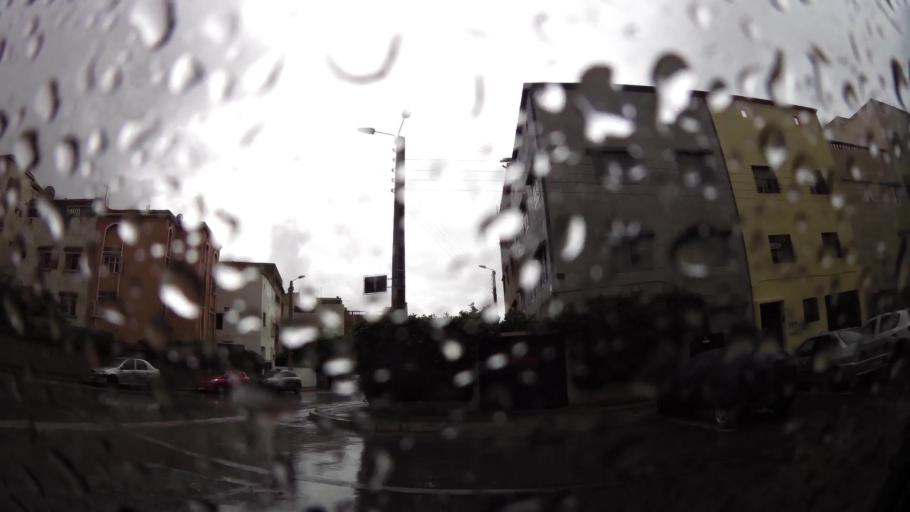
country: MA
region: Grand Casablanca
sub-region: Mediouna
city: Tit Mellil
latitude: 33.6142
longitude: -7.4976
